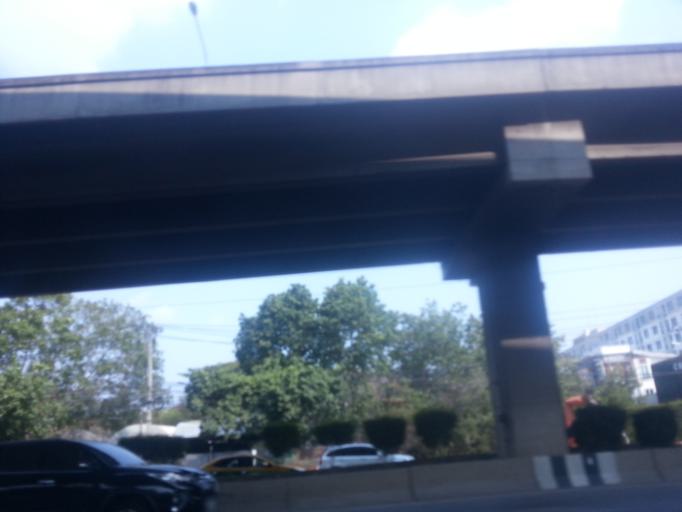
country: TH
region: Bangkok
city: Lak Si
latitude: 13.8975
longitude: 100.5915
